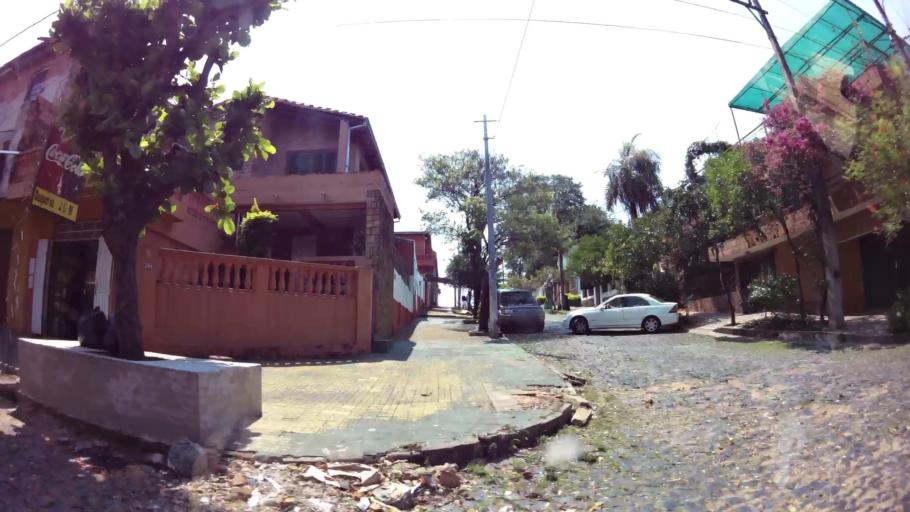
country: PY
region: Presidente Hayes
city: Nanawa
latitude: -25.2833
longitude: -57.6522
